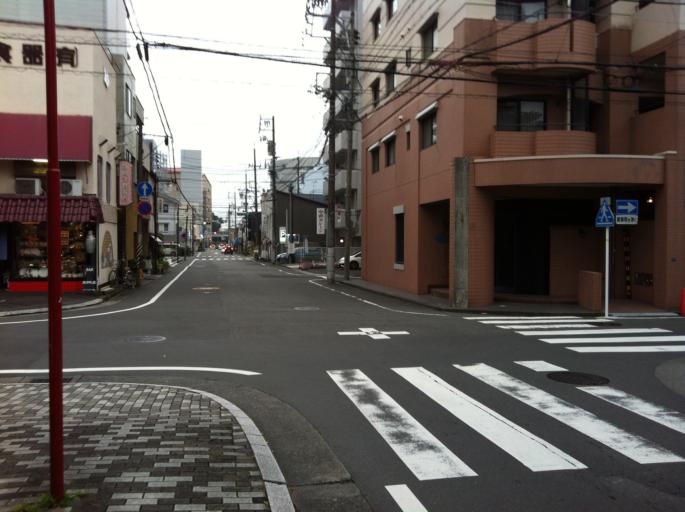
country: JP
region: Shizuoka
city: Shizuoka-shi
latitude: 34.9703
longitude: 138.3812
